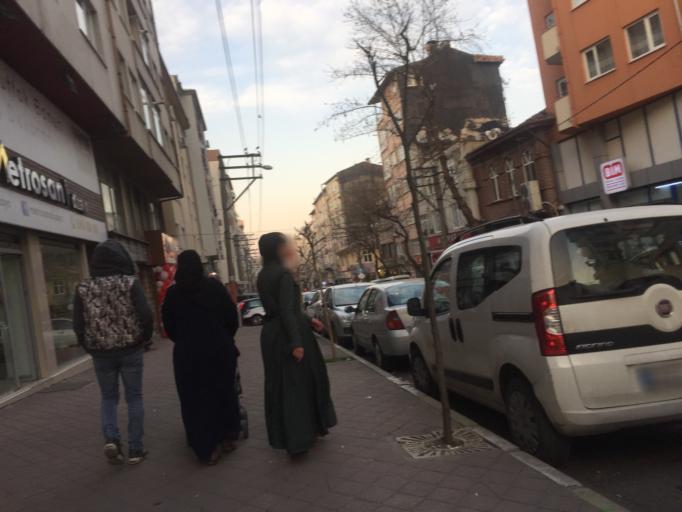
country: TR
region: Bursa
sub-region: Osmangazi
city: Bursa
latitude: 40.1873
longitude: 29.0782
